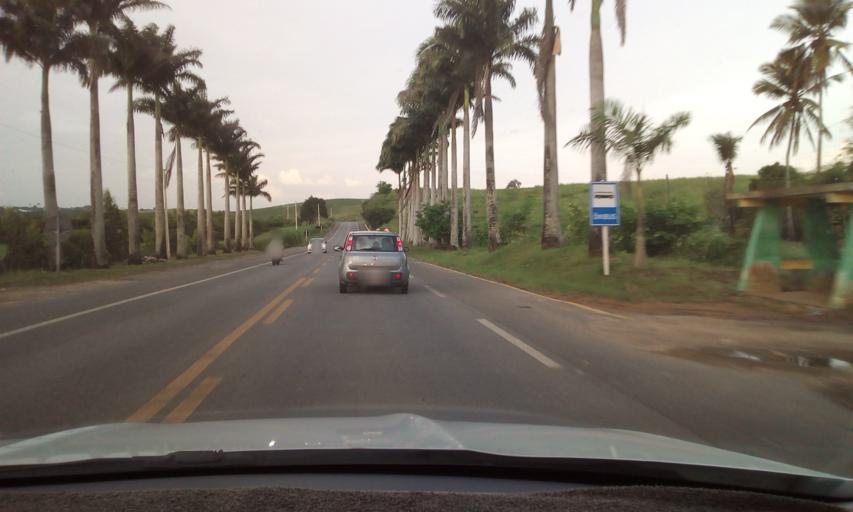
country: BR
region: Pernambuco
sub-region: Vicencia
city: Vicencia
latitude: -7.6280
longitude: -35.2458
